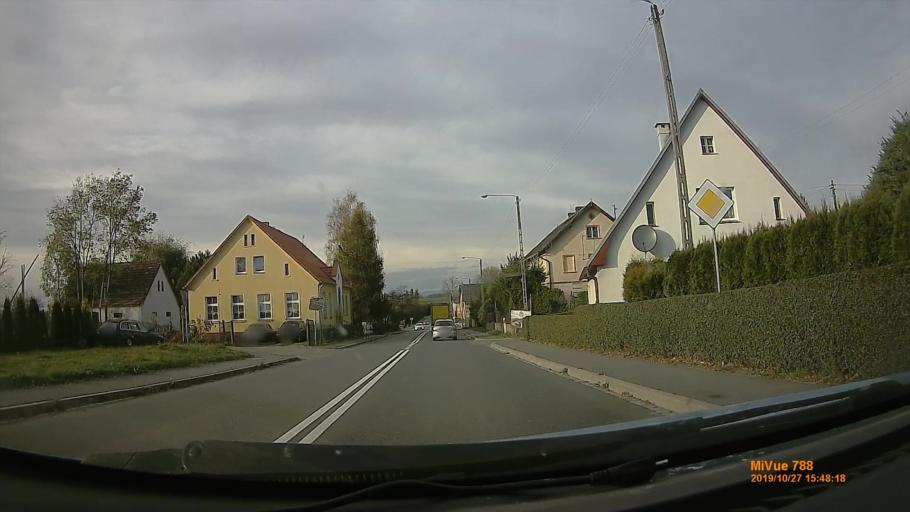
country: PL
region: Lower Silesian Voivodeship
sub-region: Powiat klodzki
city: Bozkow
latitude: 50.4964
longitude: 16.5867
